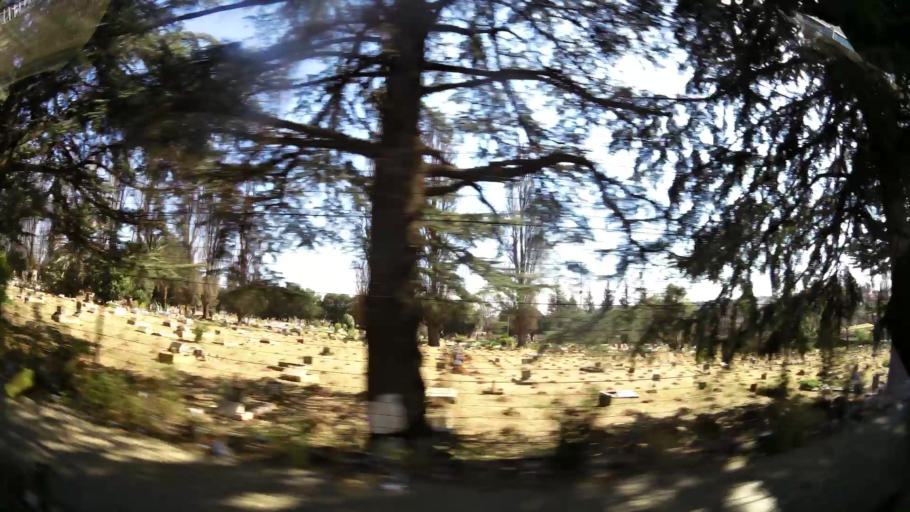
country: ZA
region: Gauteng
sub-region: City of Johannesburg Metropolitan Municipality
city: Johannesburg
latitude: -26.1933
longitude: 27.9638
